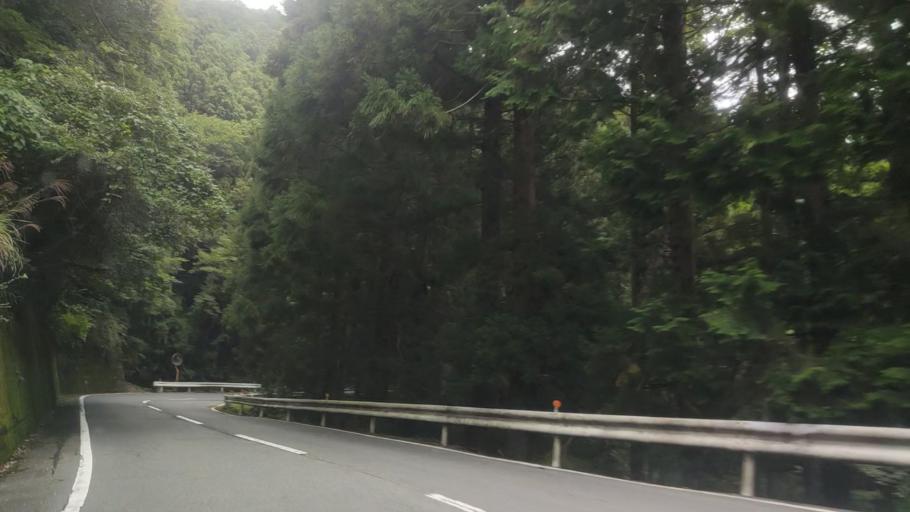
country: JP
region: Wakayama
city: Koya
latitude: 34.2111
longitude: 135.5470
